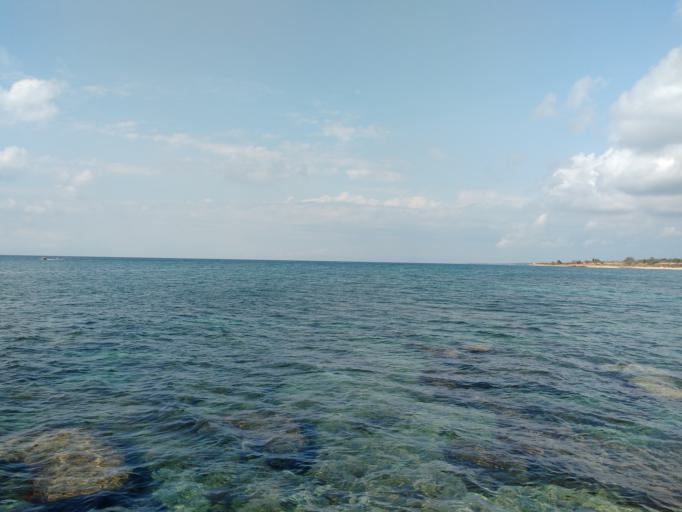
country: HR
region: Istarska
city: Novigrad
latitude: 45.3381
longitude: 13.5403
